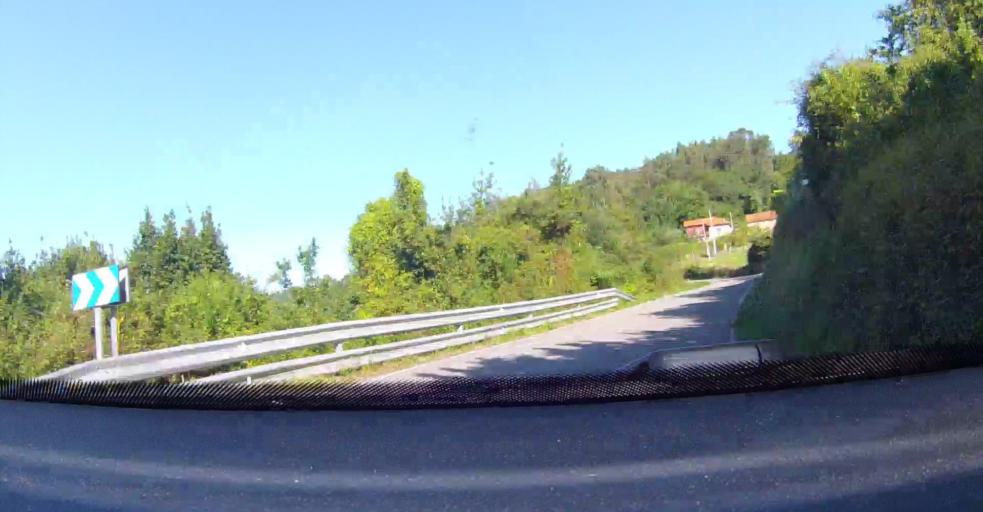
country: ES
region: Asturias
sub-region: Province of Asturias
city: Villaviciosa
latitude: 43.4863
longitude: -5.4202
